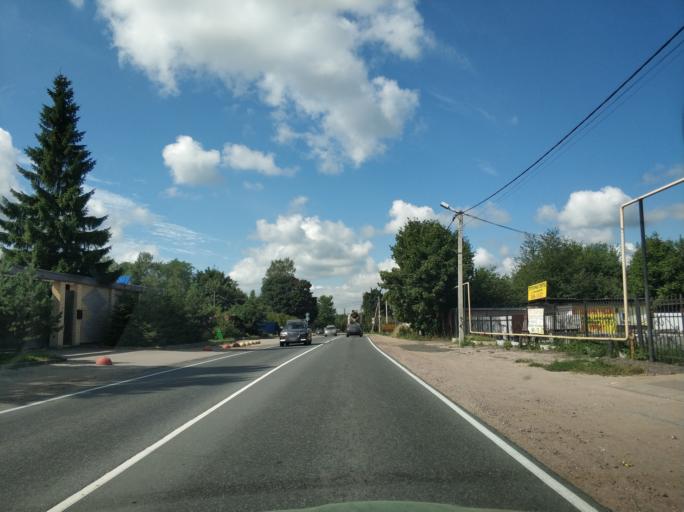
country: RU
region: Leningrad
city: Romanovka
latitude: 60.0496
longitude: 30.7159
